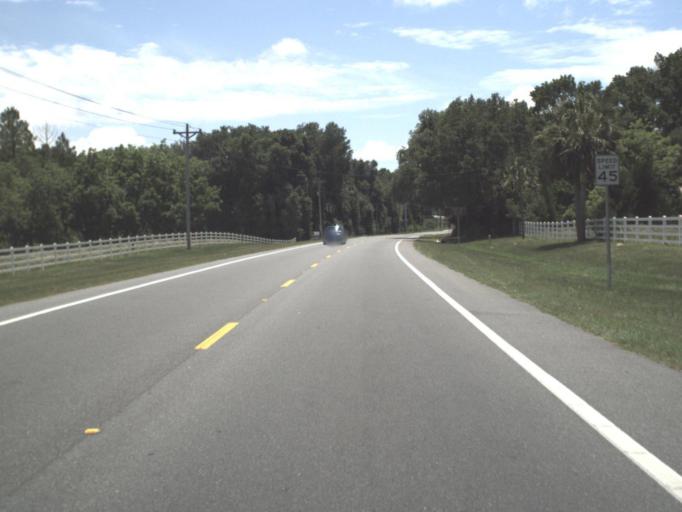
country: US
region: Florida
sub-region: Levy County
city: Manatee Road
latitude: 29.6070
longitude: -82.9824
